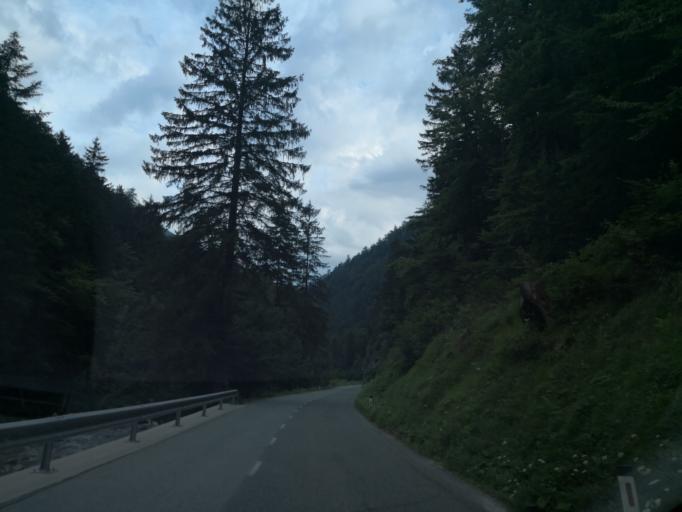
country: SI
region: Jezersko
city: Zgornje Jezersko
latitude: 46.3477
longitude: 14.4799
